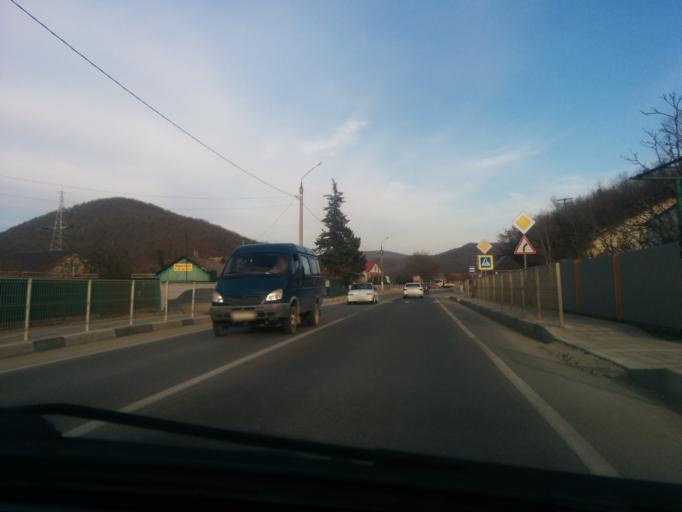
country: RU
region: Krasnodarskiy
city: Novomikhaylovskiy
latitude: 44.2584
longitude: 38.8615
